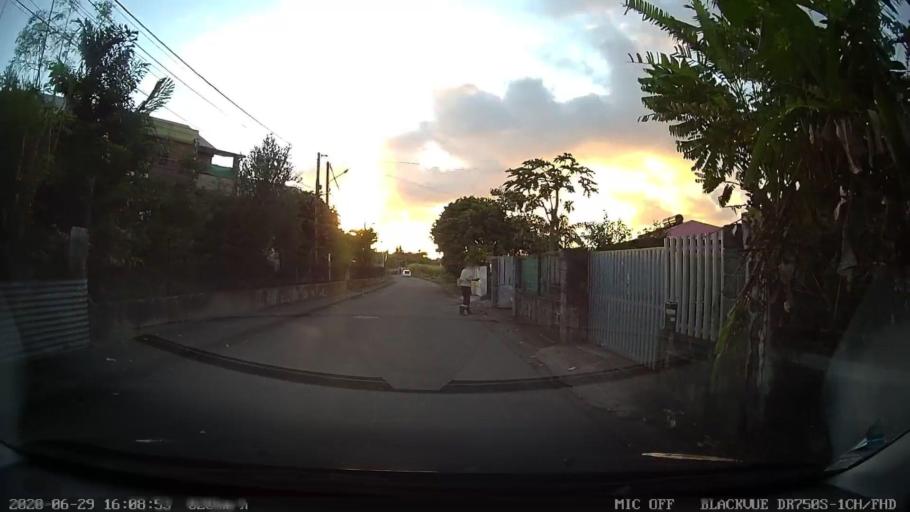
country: RE
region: Reunion
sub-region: Reunion
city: Bras-Panon
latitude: -20.9925
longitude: 55.6800
